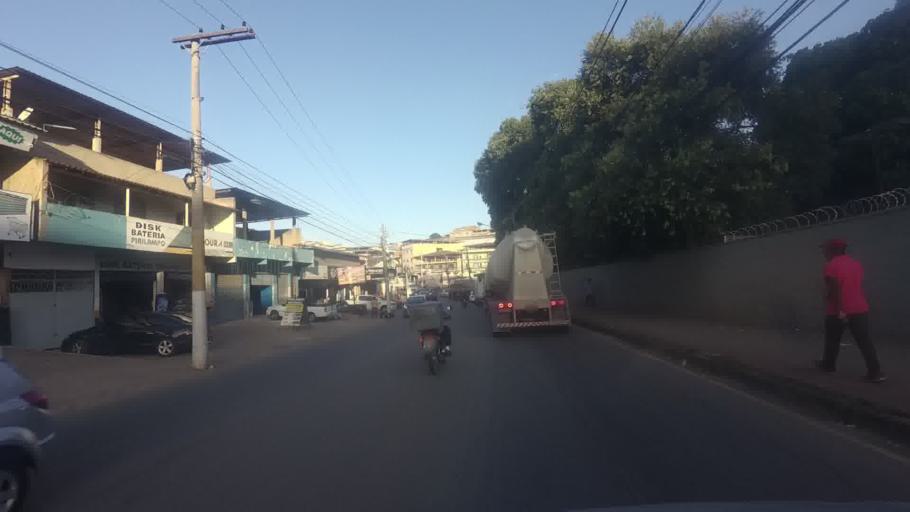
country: BR
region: Espirito Santo
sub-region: Cachoeiro De Itapemirim
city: Cachoeiro de Itapemirim
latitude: -20.8480
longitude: -41.1490
